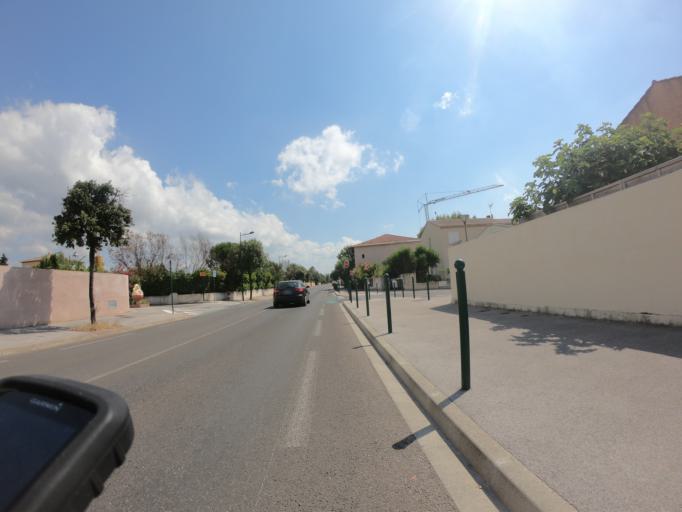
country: FR
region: Provence-Alpes-Cote d'Azur
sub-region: Departement du Var
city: La Garde
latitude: 43.1286
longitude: 6.0237
